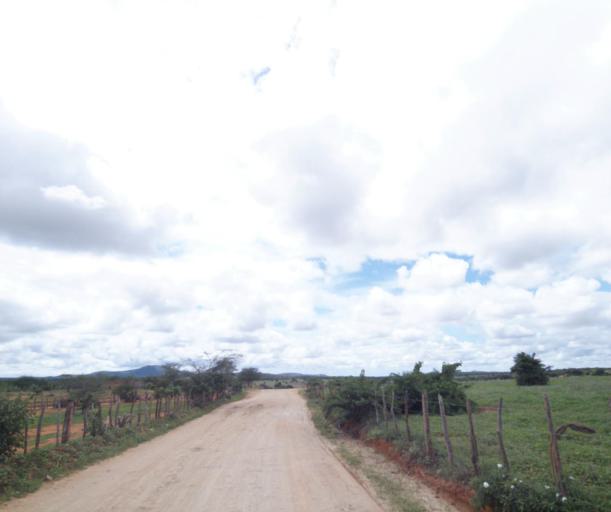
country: BR
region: Bahia
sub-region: Tanhacu
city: Tanhacu
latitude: -14.1620
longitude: -41.1729
